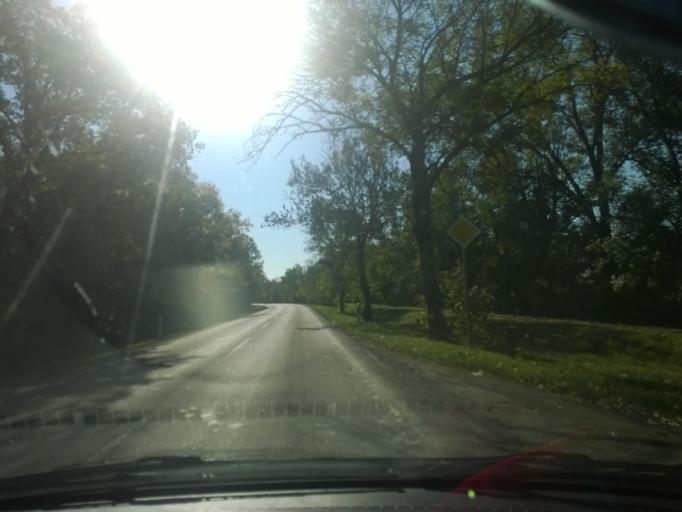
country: HU
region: Csongrad
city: Hodmezovasarhely
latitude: 46.4916
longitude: 20.3137
